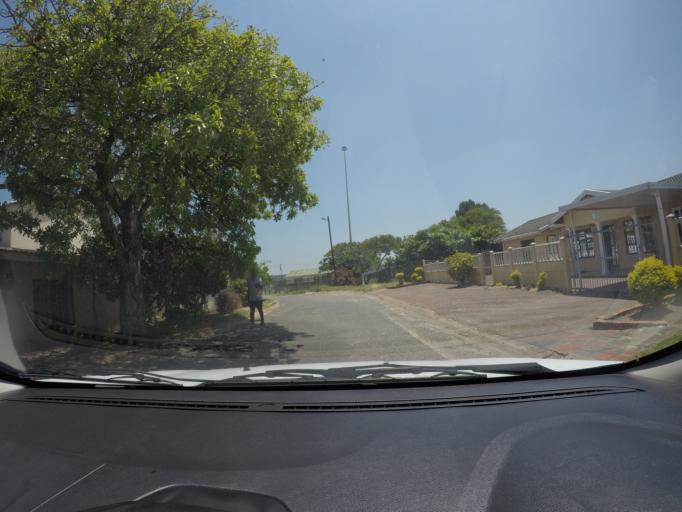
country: ZA
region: KwaZulu-Natal
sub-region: uThungulu District Municipality
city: eSikhawini
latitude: -28.8747
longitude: 31.9085
